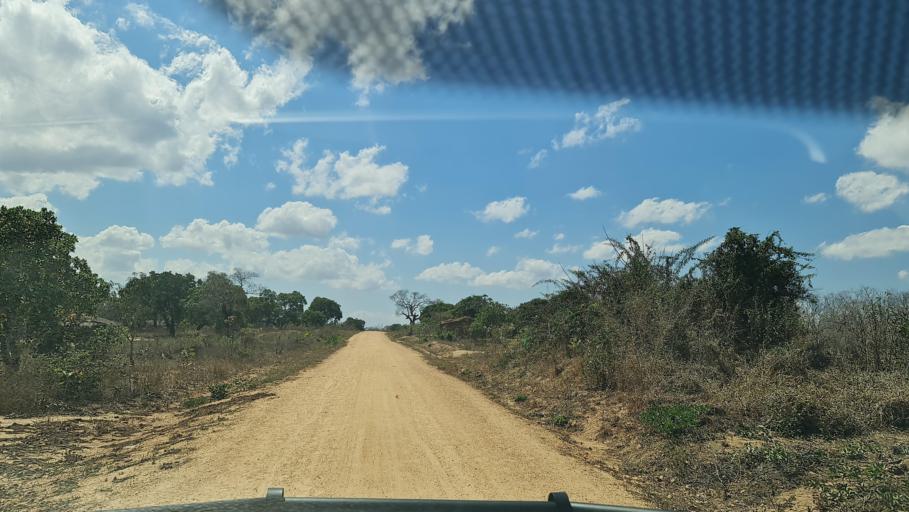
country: MZ
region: Nampula
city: Nacala
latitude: -14.1788
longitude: 40.2196
